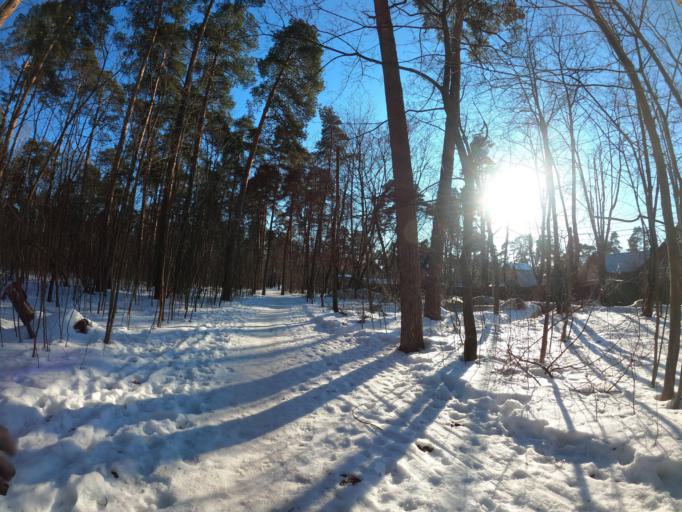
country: RU
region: Moskovskaya
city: Udel'naya
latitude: 55.6389
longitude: 37.9990
